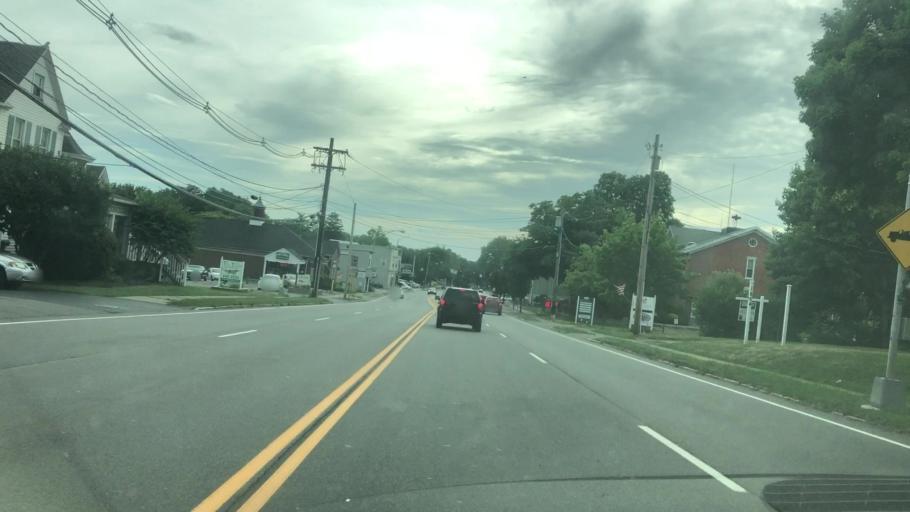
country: US
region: New York
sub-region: Monroe County
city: East Rochester
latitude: 43.1308
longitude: -77.4735
